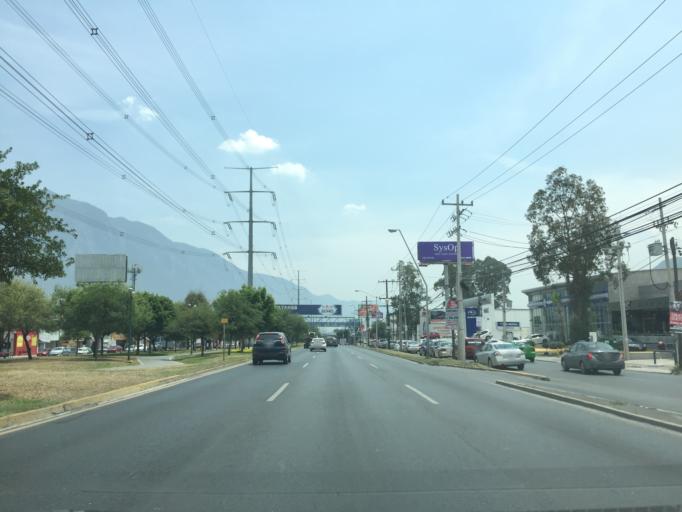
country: MX
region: Nuevo Leon
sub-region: Monterrey
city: Monterrey
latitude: 25.6259
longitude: -100.2932
